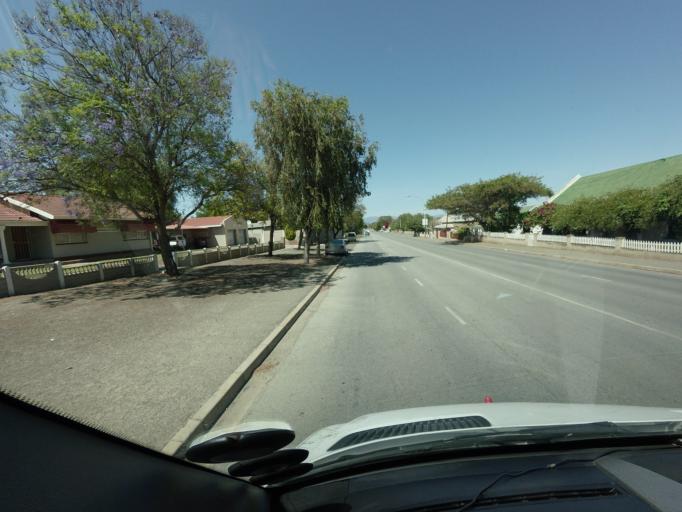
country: ZA
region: Western Cape
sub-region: Eden District Municipality
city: Oudtshoorn
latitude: -33.5779
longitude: 22.2056
